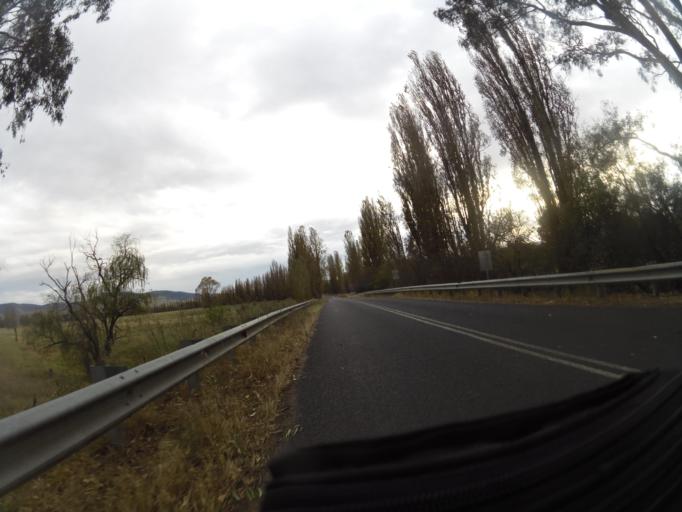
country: AU
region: New South Wales
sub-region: Greater Hume Shire
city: Holbrook
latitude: -36.0451
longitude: 147.9333
